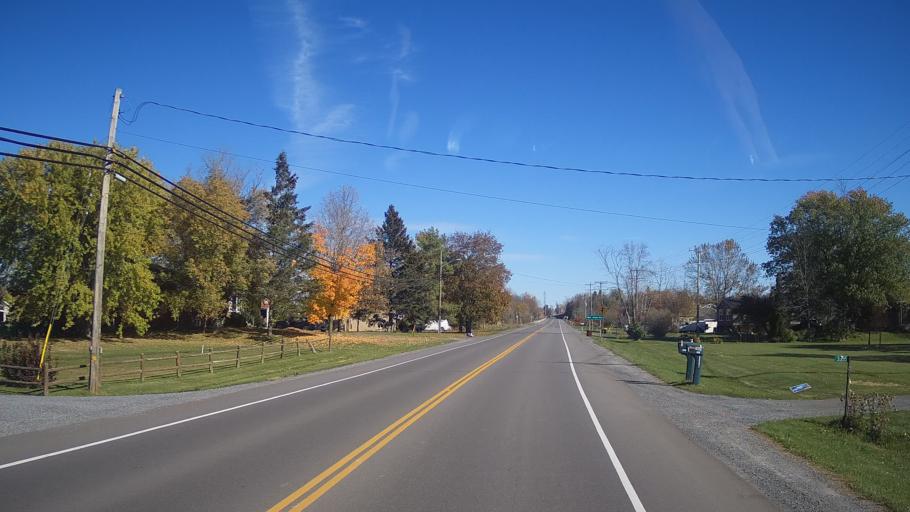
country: CA
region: Ontario
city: Kingston
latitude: 44.4060
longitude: -76.6579
